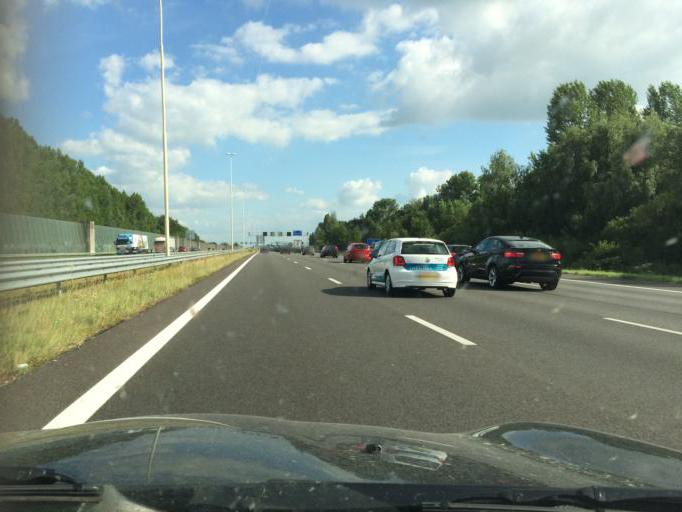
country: NL
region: Utrecht
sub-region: Gemeente Nieuwegein
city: Nieuwegein
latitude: 52.0100
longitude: 5.0716
